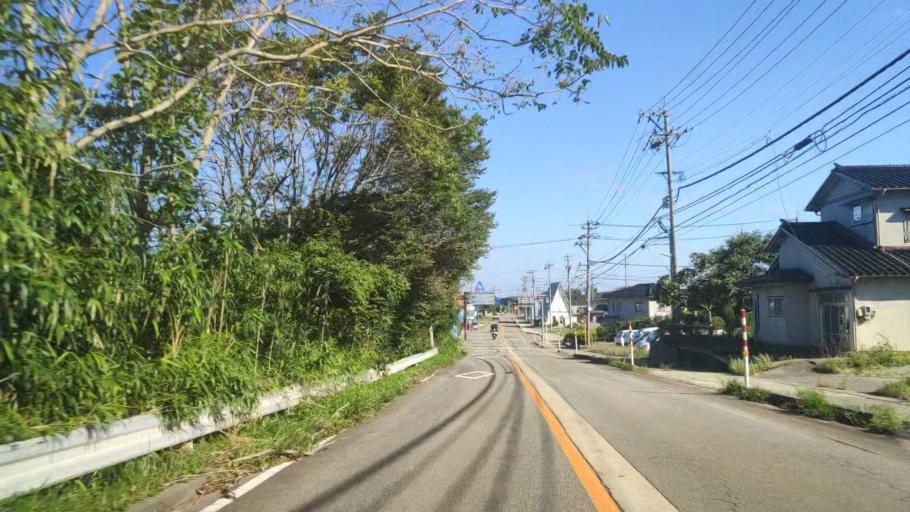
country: JP
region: Ishikawa
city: Hakui
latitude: 36.9933
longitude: 136.7767
